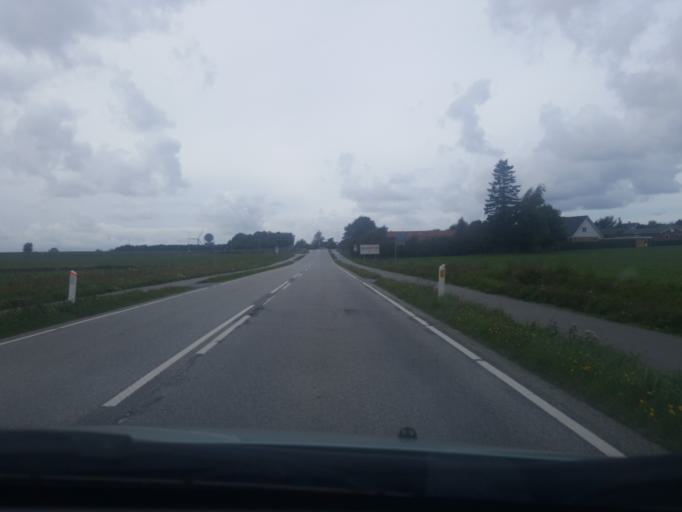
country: DK
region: Zealand
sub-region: Guldborgsund Kommune
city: Nykobing Falster
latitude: 54.7046
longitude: 11.9229
